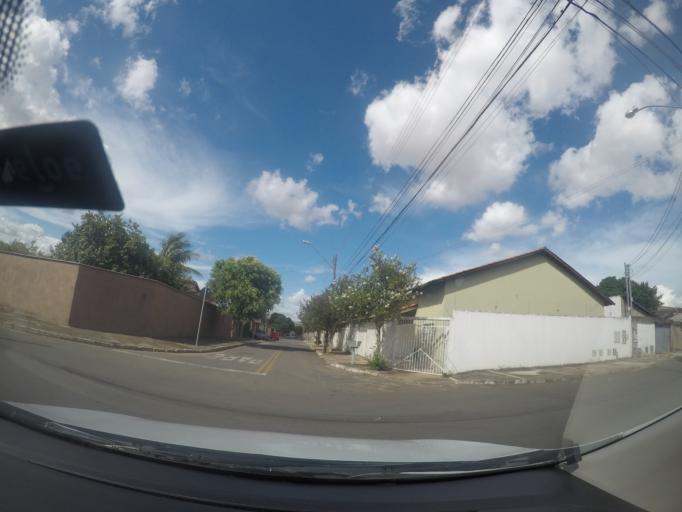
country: BR
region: Goias
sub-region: Goiania
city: Goiania
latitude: -16.6764
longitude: -49.3005
